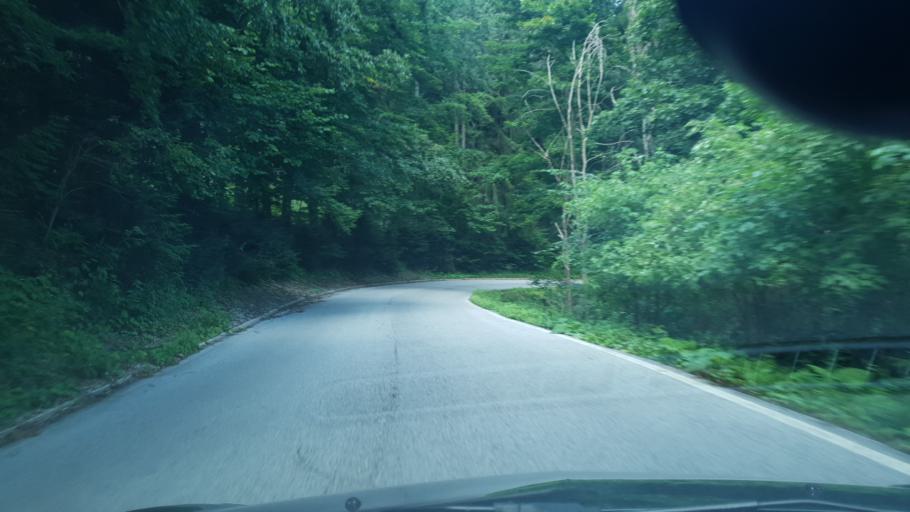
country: HR
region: Grad Zagreb
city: Kasina
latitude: 45.9063
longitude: 15.9736
